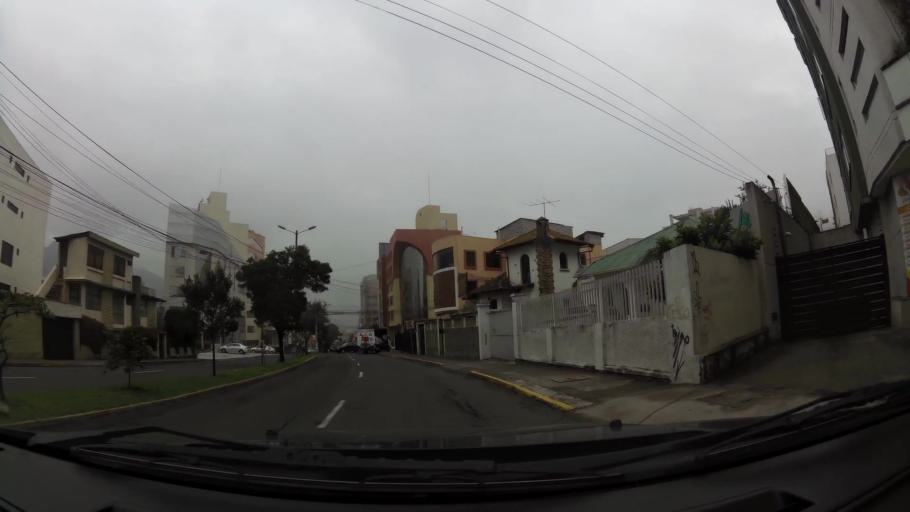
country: EC
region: Pichincha
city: Quito
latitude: -0.2066
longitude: -78.4819
